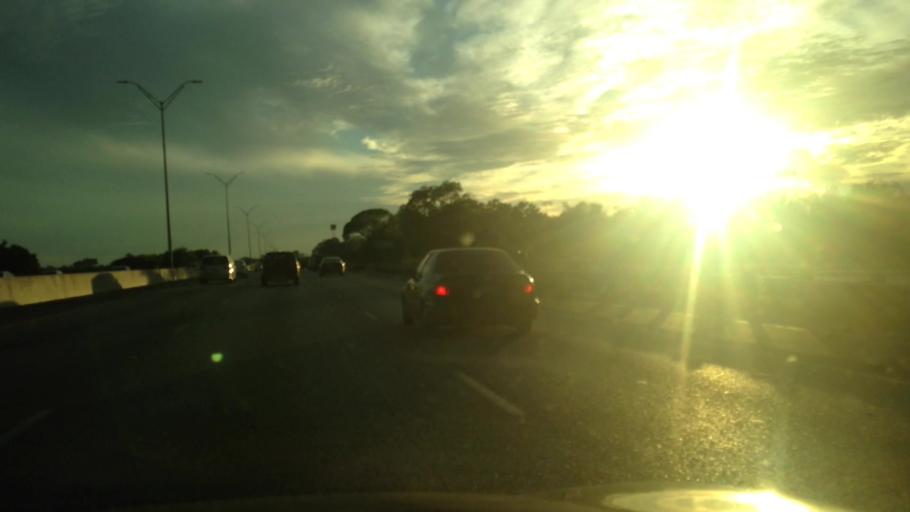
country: US
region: Texas
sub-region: Hays County
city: San Marcos
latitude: 29.8763
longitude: -97.9299
